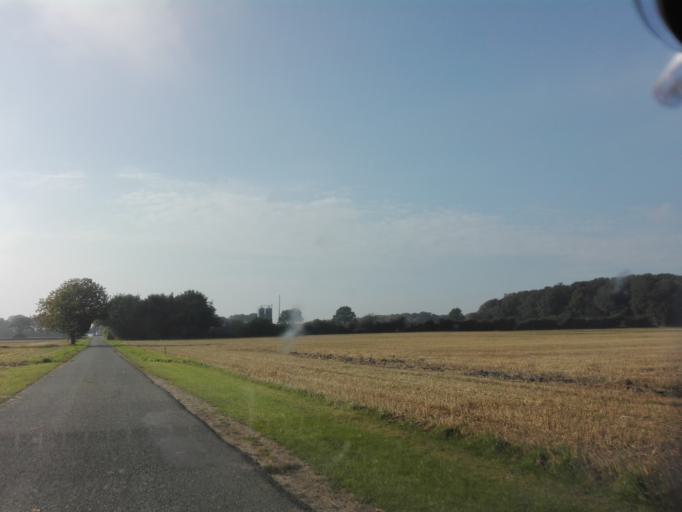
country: DK
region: Central Jutland
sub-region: Odder Kommune
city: Odder
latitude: 55.8717
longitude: 10.1628
